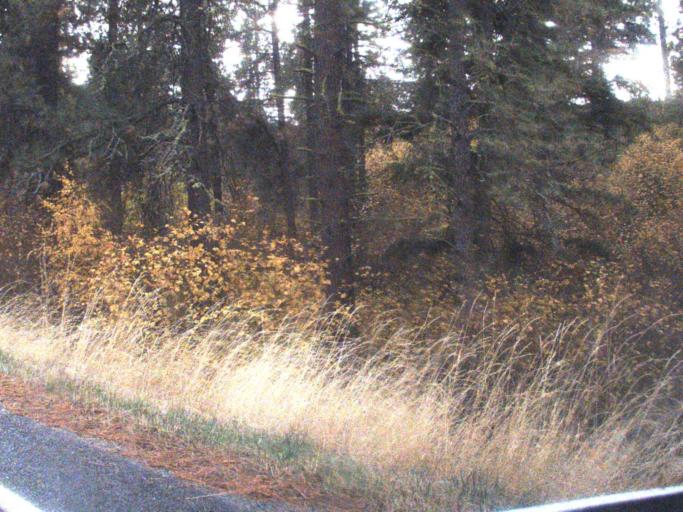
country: US
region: Washington
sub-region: Stevens County
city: Kettle Falls
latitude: 48.4800
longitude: -118.1714
